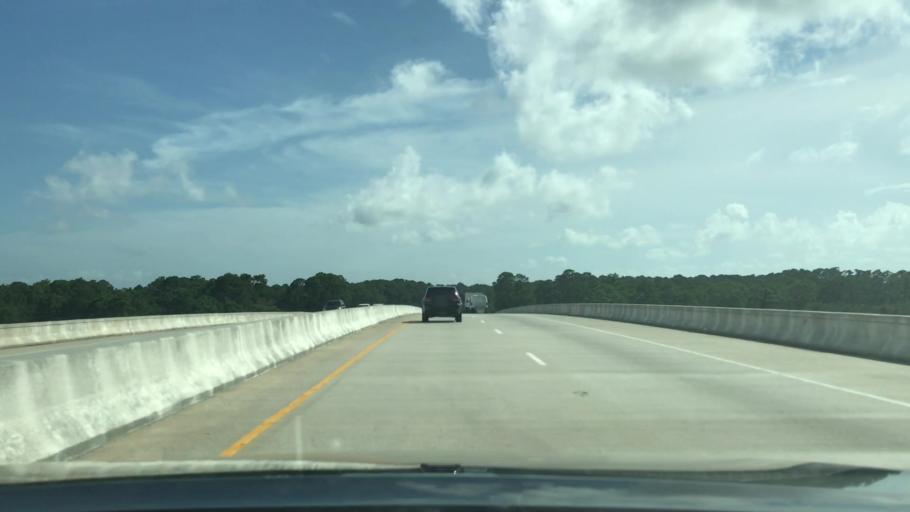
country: US
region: South Carolina
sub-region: Beaufort County
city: Hilton Head Island
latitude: 32.1783
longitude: -80.7689
